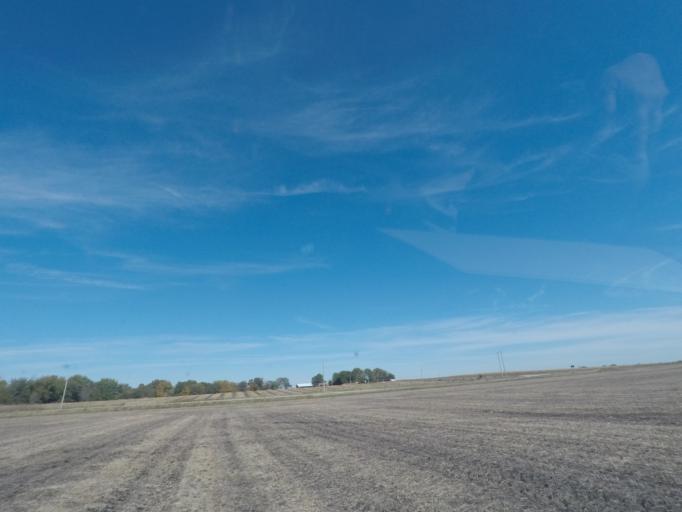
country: US
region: Iowa
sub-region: Story County
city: Nevada
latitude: 42.0407
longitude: -93.3609
